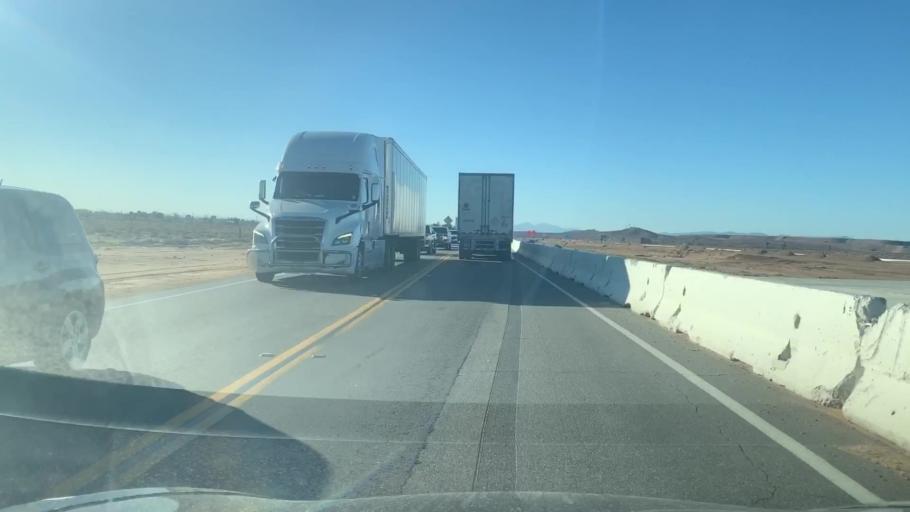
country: US
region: California
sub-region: Kern County
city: Boron
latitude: 35.0100
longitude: -117.6270
